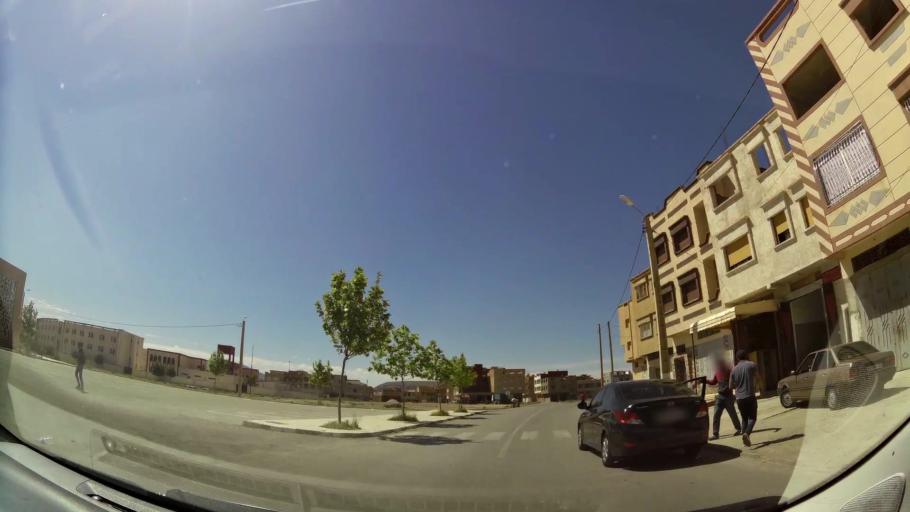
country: MA
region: Oriental
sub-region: Oujda-Angad
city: Oujda
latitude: 34.6621
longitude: -1.8758
